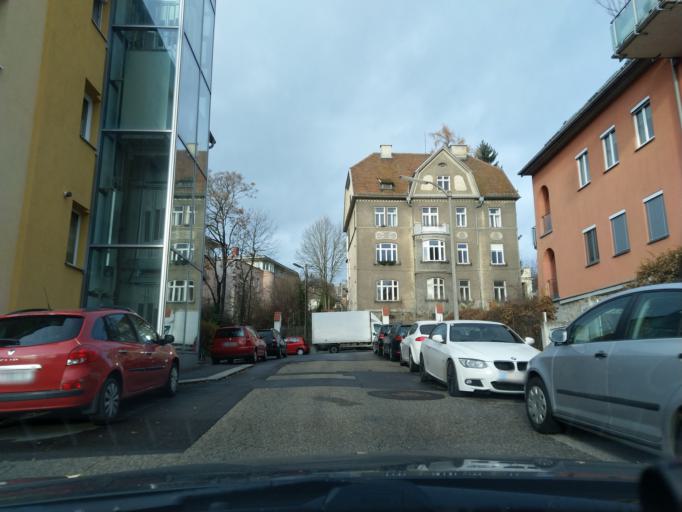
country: AT
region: Upper Austria
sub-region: Linz Stadt
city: Linz
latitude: 48.3134
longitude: 14.2765
